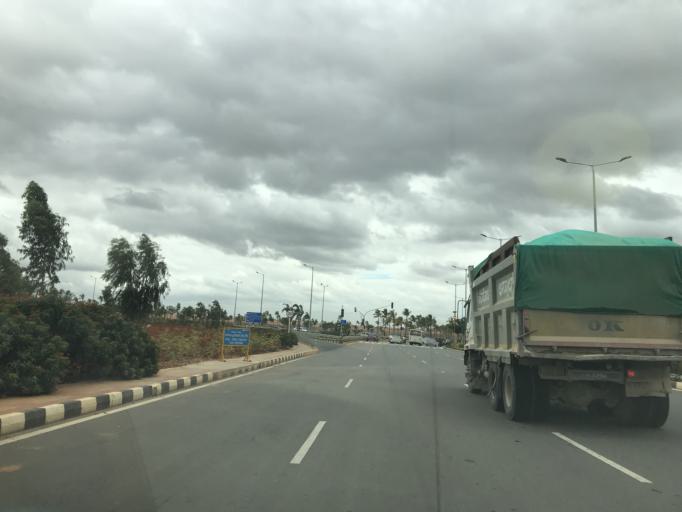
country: IN
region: Karnataka
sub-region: Bangalore Rural
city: Devanhalli
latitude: 13.1959
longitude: 77.6806
